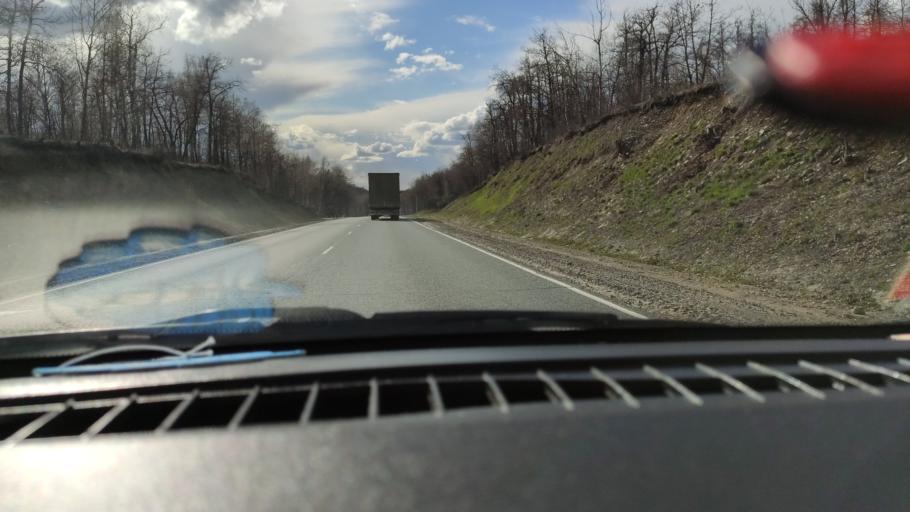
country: RU
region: Saratov
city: Vol'sk
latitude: 52.1110
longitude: 47.3449
